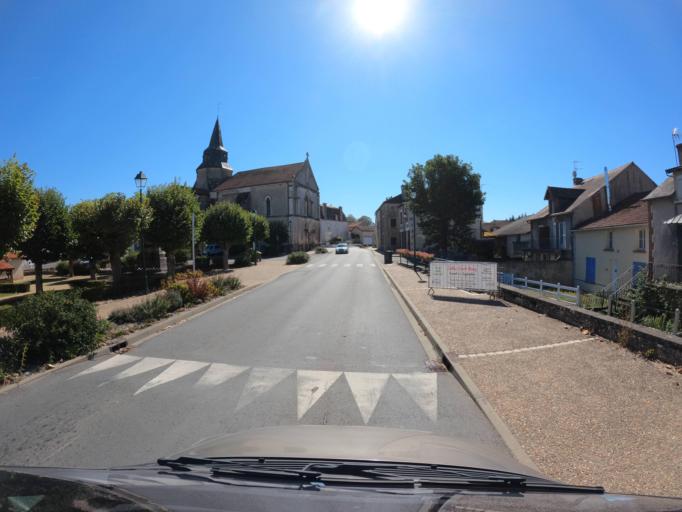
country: FR
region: Poitou-Charentes
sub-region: Departement de la Vienne
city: Lathus-Saint-Remy
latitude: 46.3340
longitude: 0.9584
